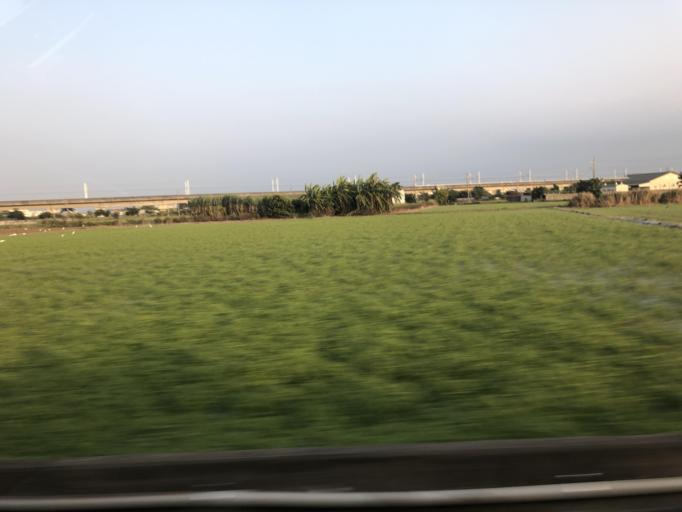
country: TW
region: Taiwan
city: Xinying
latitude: 23.1498
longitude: 120.2736
